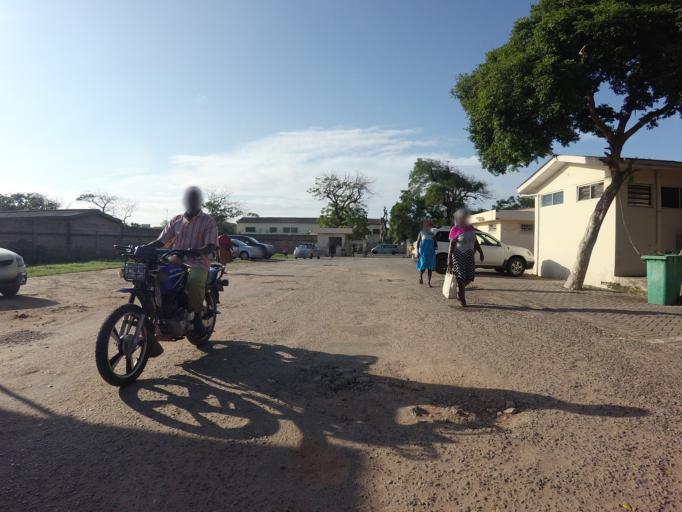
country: GH
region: Greater Accra
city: Accra
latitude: 5.5375
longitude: -0.2231
